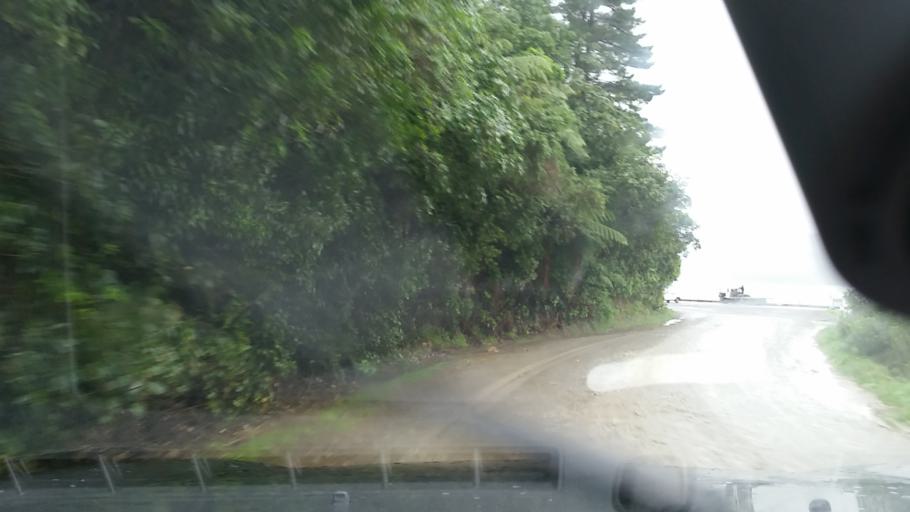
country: NZ
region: Marlborough
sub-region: Marlborough District
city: Picton
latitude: -41.3014
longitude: 174.1137
